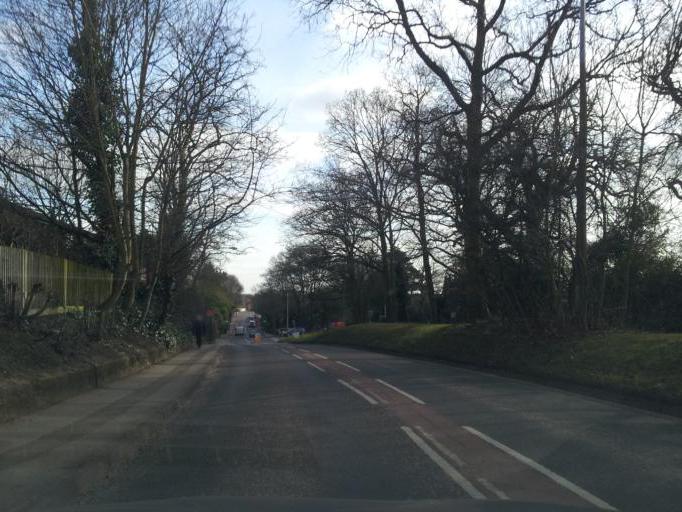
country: GB
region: England
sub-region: Hertfordshire
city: St Albans
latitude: 51.7583
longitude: -0.3267
